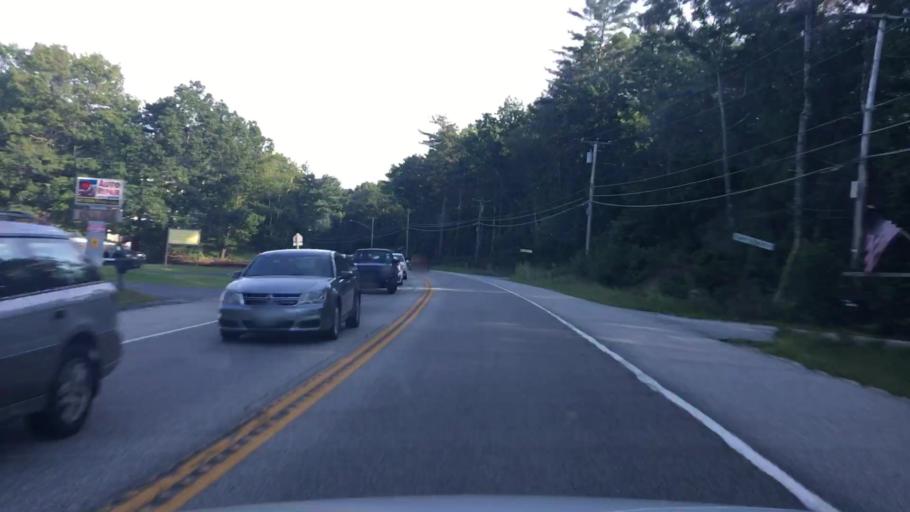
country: US
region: Maine
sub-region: Cumberland County
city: North Windham
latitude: 43.8624
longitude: -70.4653
